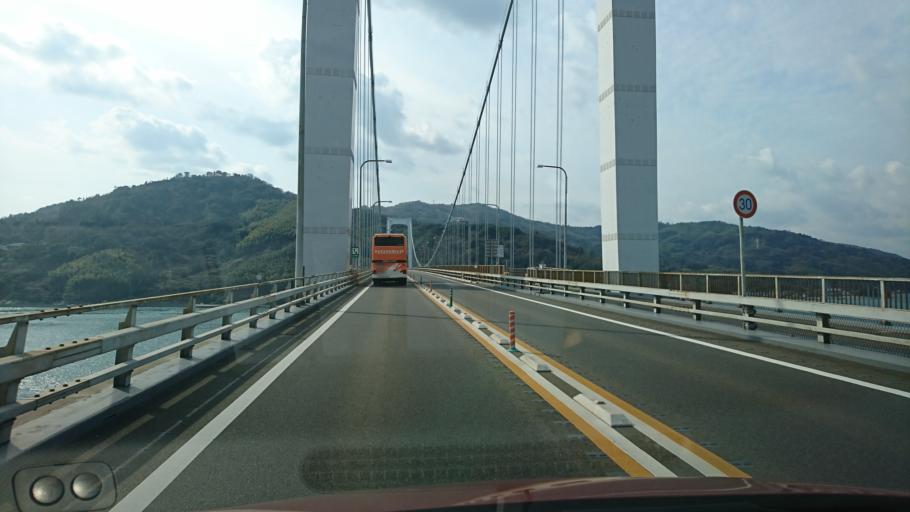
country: JP
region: Hiroshima
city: Innoshima
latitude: 34.1945
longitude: 133.0747
